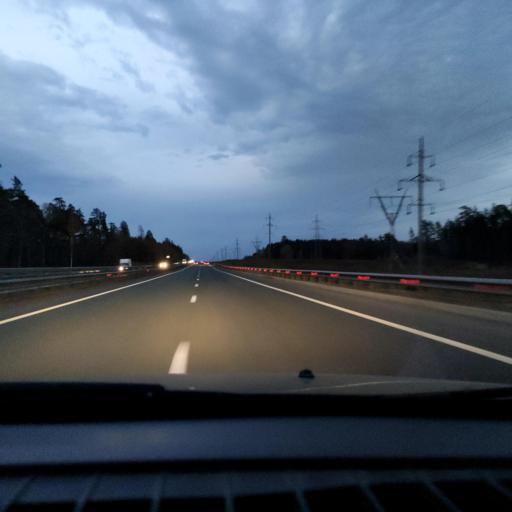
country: RU
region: Samara
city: Povolzhskiy
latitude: 53.5174
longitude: 49.7695
